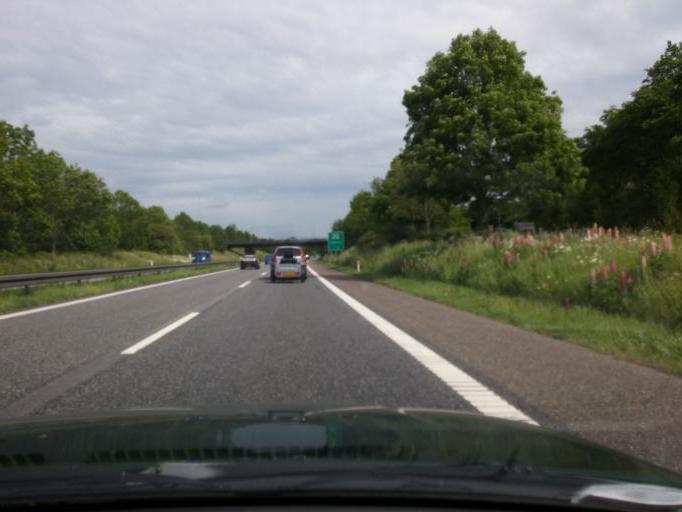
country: DK
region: South Denmark
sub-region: Odense Kommune
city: Bellinge
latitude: 55.3617
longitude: 10.3418
